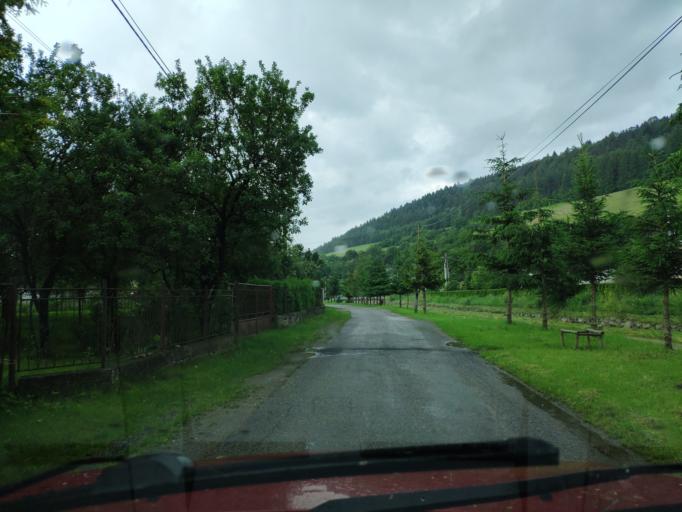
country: SK
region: Presovsky
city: Sabinov
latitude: 49.0212
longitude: 21.0243
